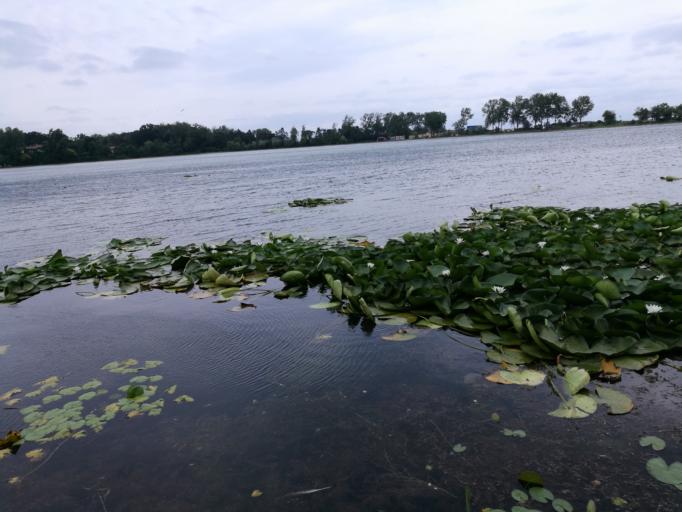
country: RO
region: Constanta
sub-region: Comuna Douazeci si Trei August
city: Douazeci si Trei August
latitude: 43.8669
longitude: 28.6010
